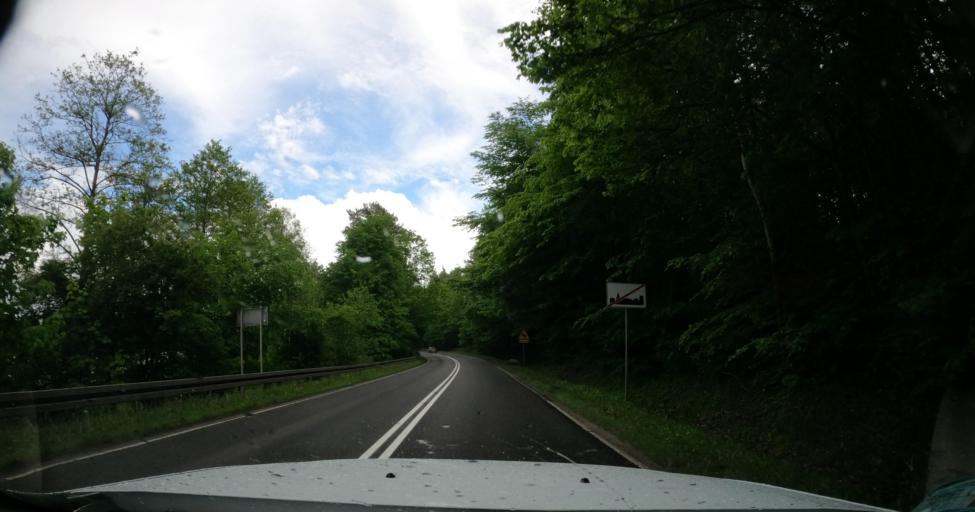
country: PL
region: Pomeranian Voivodeship
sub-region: Powiat kartuski
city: Przodkowo
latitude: 54.3214
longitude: 18.3031
